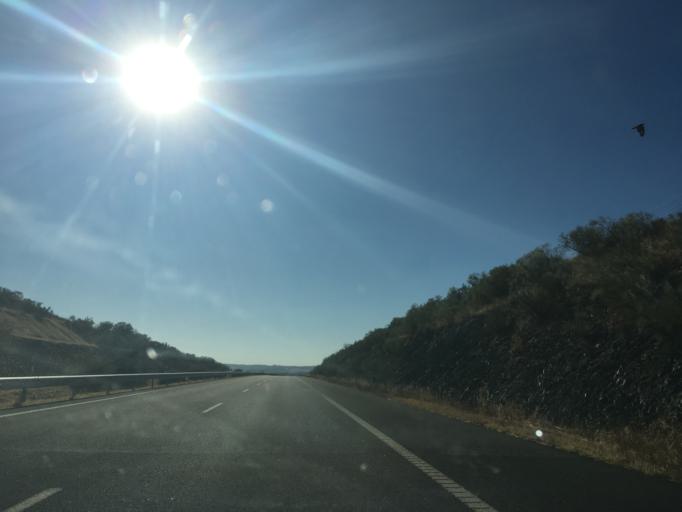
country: PT
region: Evora
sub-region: Vila Vicosa
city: Vila Vicosa
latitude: 38.8522
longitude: -7.3401
